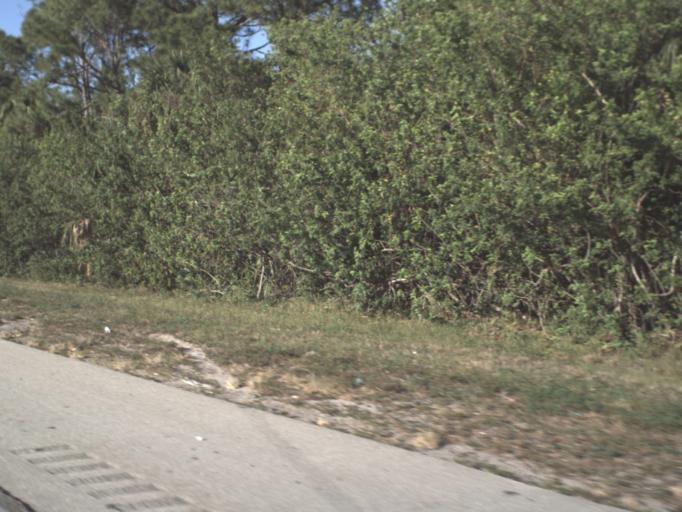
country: US
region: Florida
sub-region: Brevard County
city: June Park
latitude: 28.1530
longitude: -80.7058
